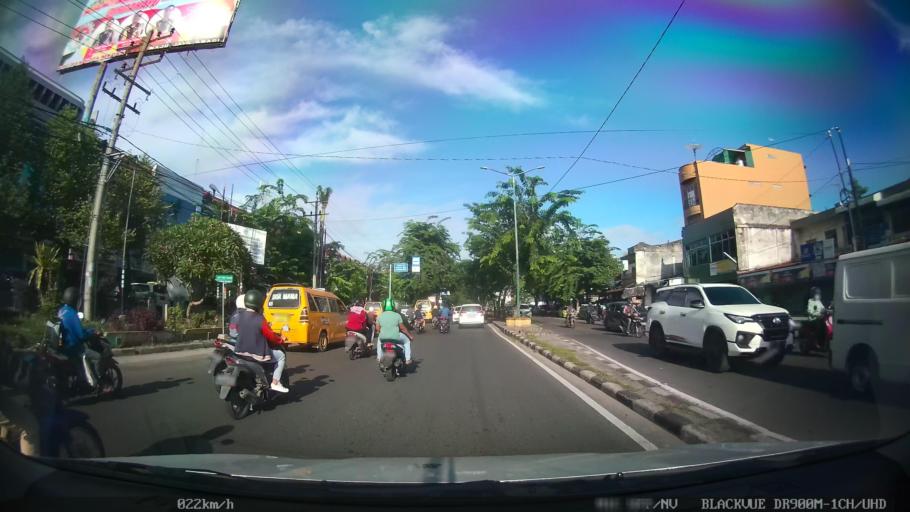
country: ID
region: North Sumatra
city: Medan
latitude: 3.5907
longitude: 98.6436
